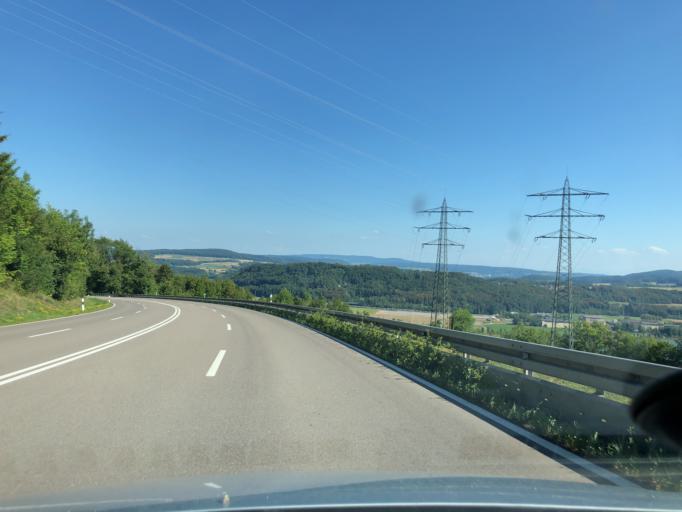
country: DE
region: Baden-Wuerttemberg
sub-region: Freiburg Region
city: Dogern
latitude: 47.6234
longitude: 8.1862
